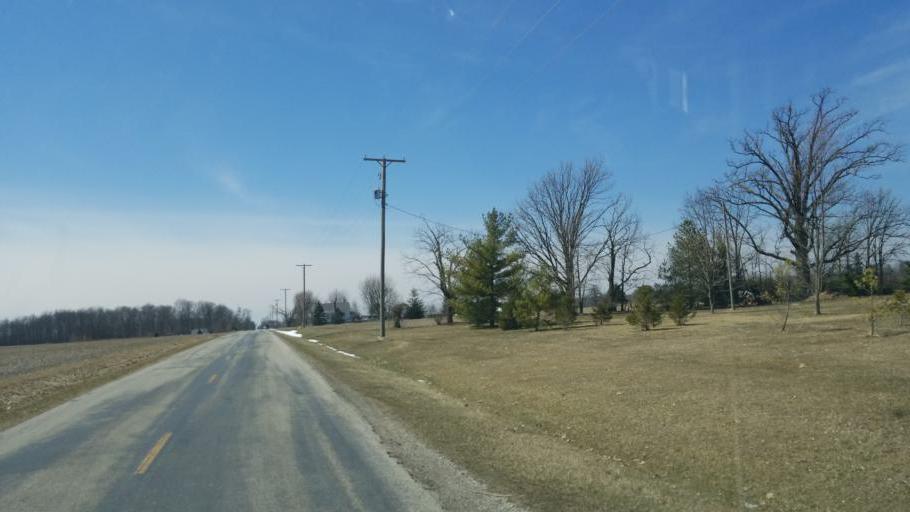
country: US
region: Ohio
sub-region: Crawford County
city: Galion
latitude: 40.6756
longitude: -82.8723
